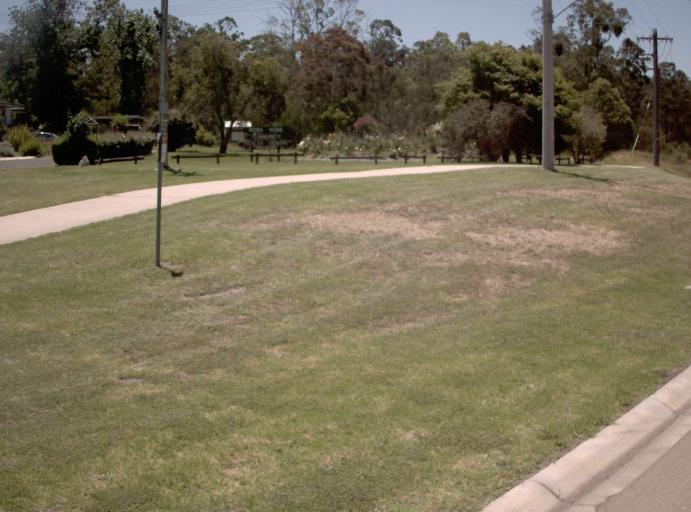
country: AU
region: Victoria
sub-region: East Gippsland
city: Lakes Entrance
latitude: -37.7313
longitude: 148.0928
